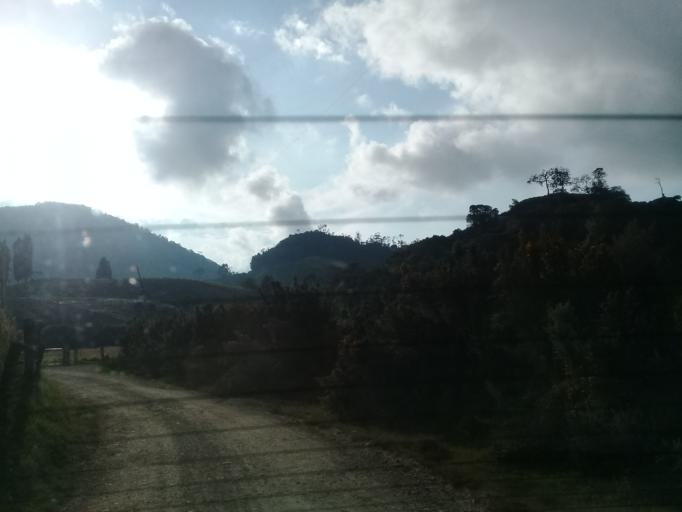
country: CO
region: Cundinamarca
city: Sibate
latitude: 4.4352
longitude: -74.2869
